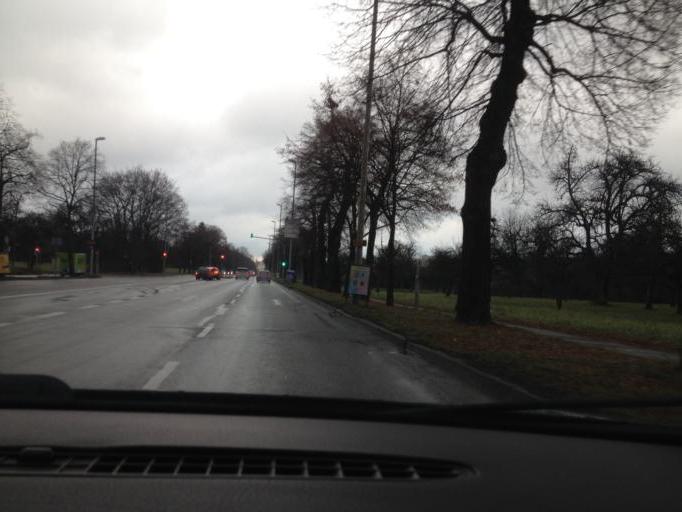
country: DE
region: Baden-Wuerttemberg
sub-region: Regierungsbezirk Stuttgart
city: Ludwigsburg
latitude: 48.9044
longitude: 9.1772
